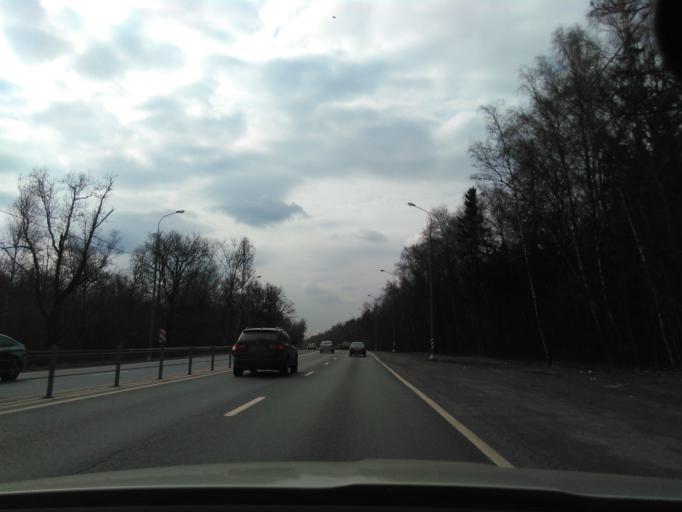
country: RU
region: Moskovskaya
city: Marfino
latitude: 56.0316
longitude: 37.5424
